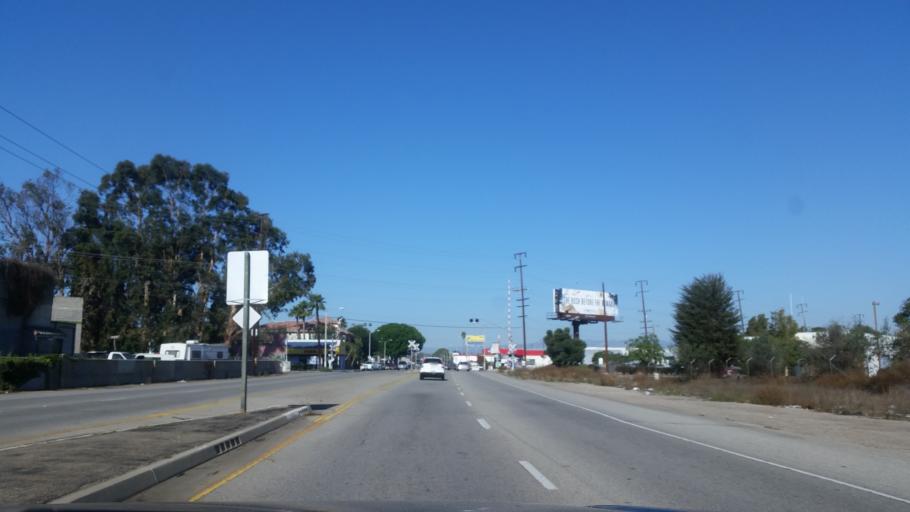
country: US
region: California
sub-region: Ventura County
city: Oxnard
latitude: 34.1820
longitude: -119.1675
